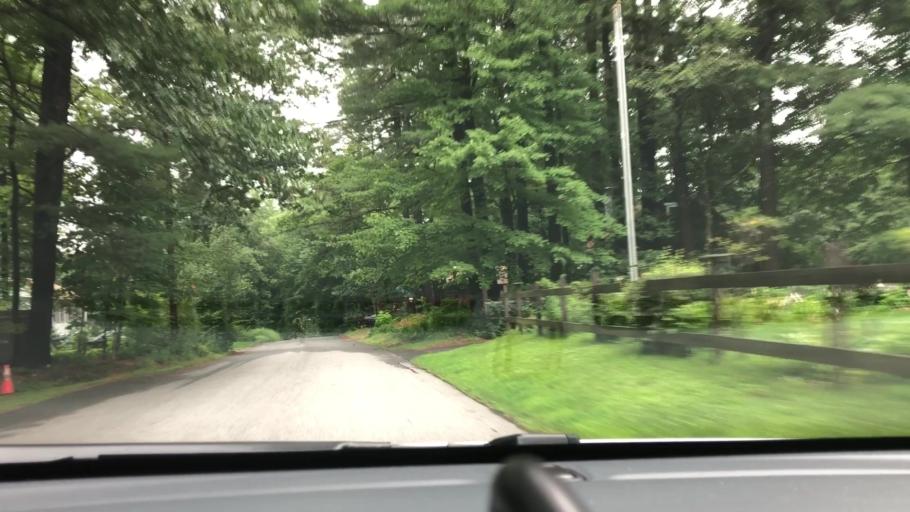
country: US
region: New Hampshire
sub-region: Hillsborough County
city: Pinardville
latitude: 43.0076
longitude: -71.5191
